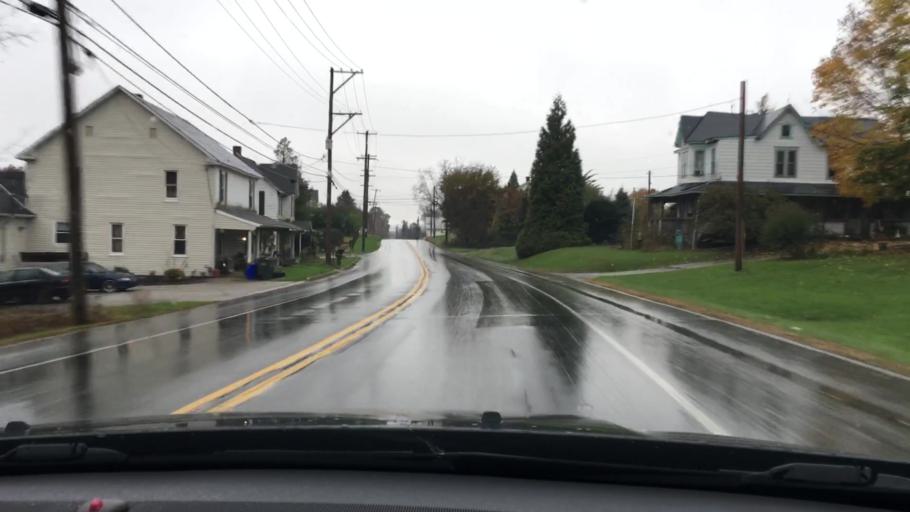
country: US
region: Pennsylvania
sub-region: York County
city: Susquehanna Trails
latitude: 39.8047
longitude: -76.3696
